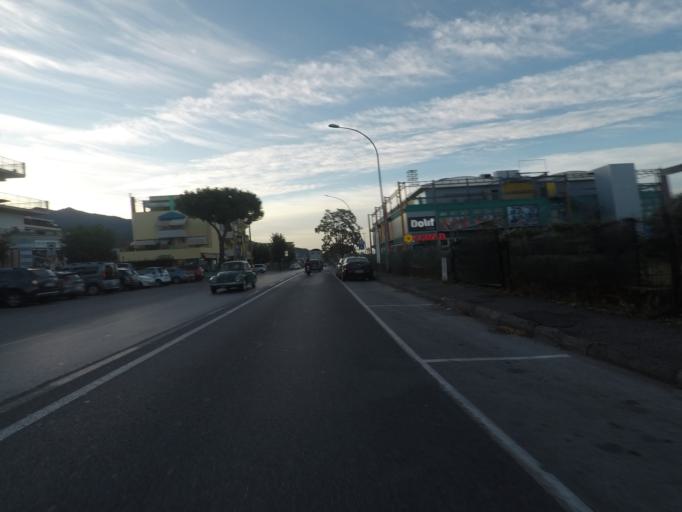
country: IT
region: Tuscany
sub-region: Provincia di Massa-Carrara
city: Massa
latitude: 44.0267
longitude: 10.1334
